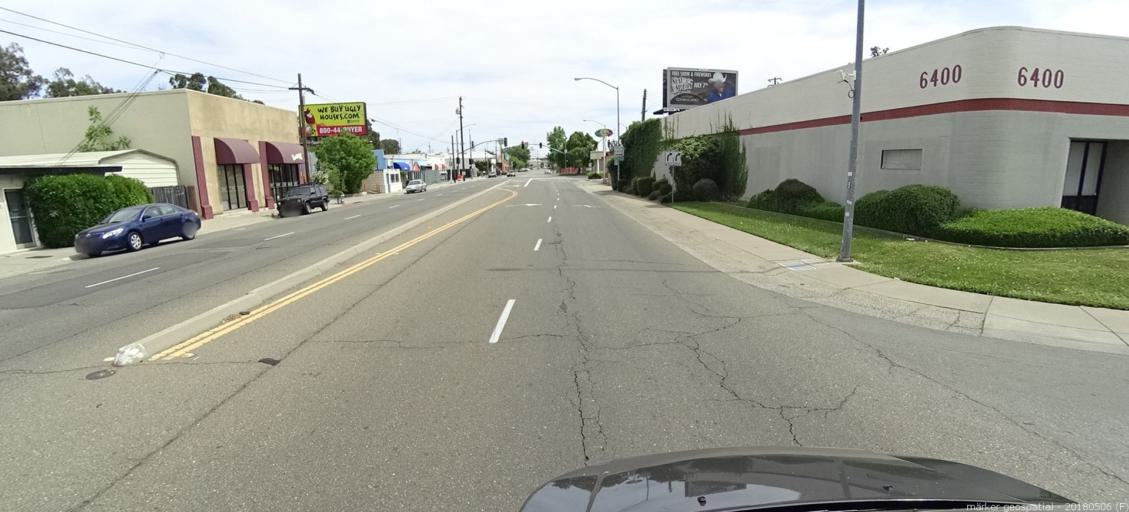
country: US
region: California
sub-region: Sacramento County
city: Rosemont
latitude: 38.5570
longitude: -121.4274
